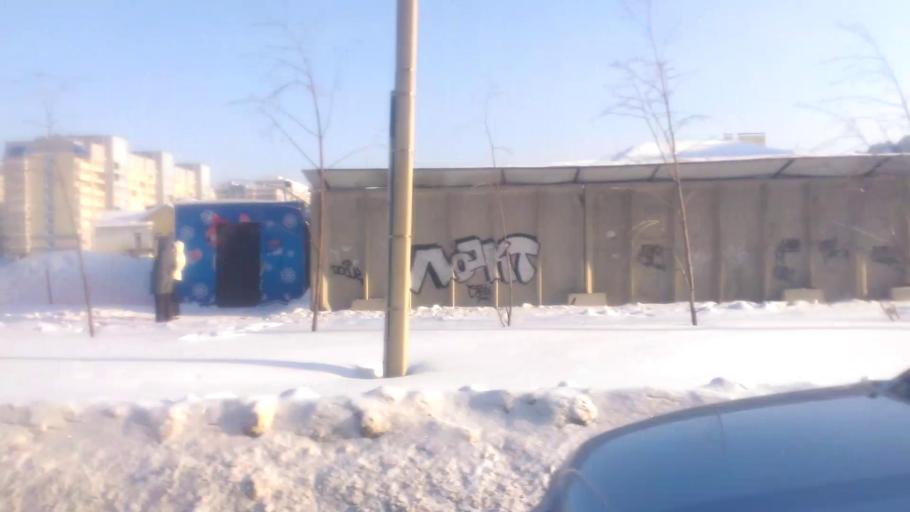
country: RU
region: Altai Krai
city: Novosilikatnyy
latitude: 53.3431
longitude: 83.6555
